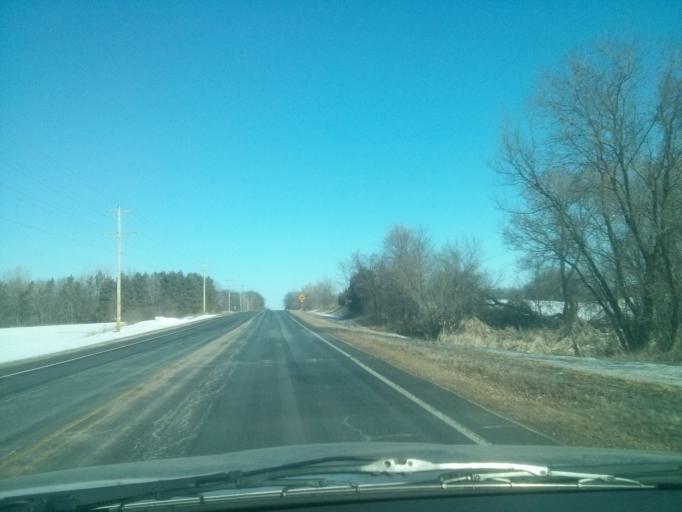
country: US
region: Minnesota
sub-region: Washington County
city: Bayport
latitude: 45.0764
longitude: -92.7360
